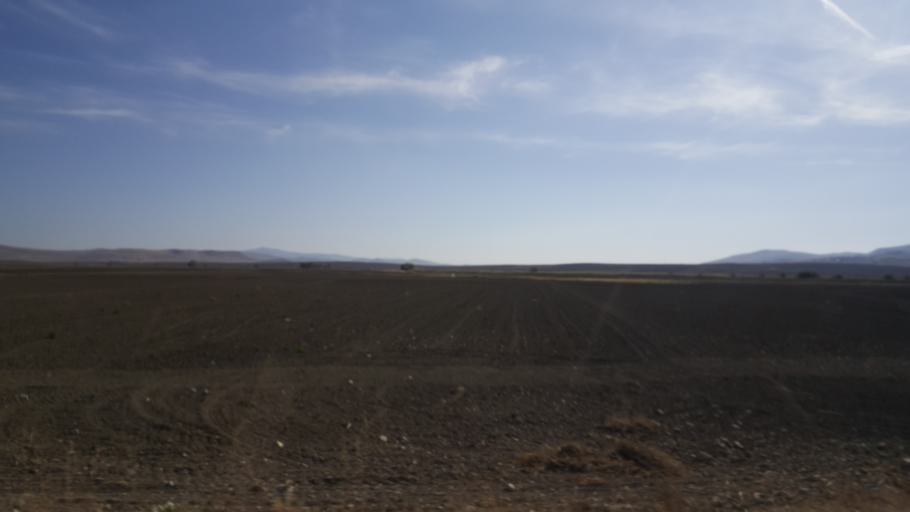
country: TR
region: Ankara
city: Yenice
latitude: 39.3788
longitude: 32.7541
